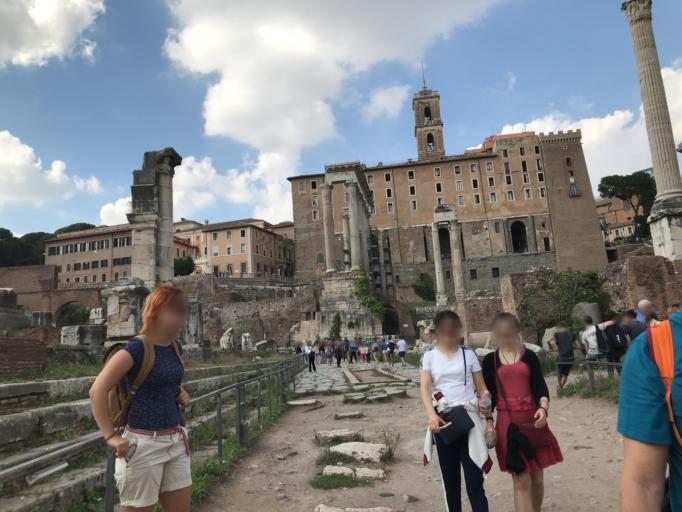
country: IT
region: Latium
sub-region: Citta metropolitana di Roma Capitale
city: Rome
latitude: 41.8922
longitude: 12.4851
